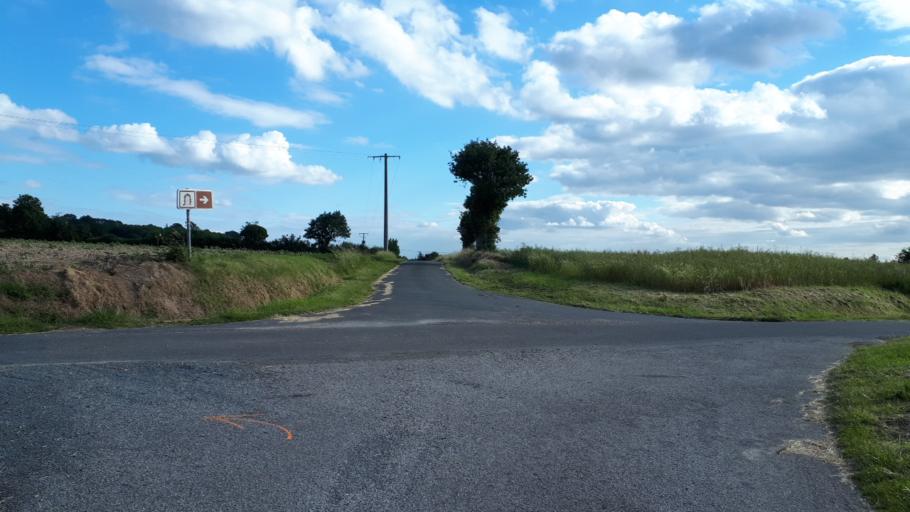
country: FR
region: Centre
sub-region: Departement du Loir-et-Cher
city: Sarge-sur-Braye
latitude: 47.9277
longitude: 0.8619
